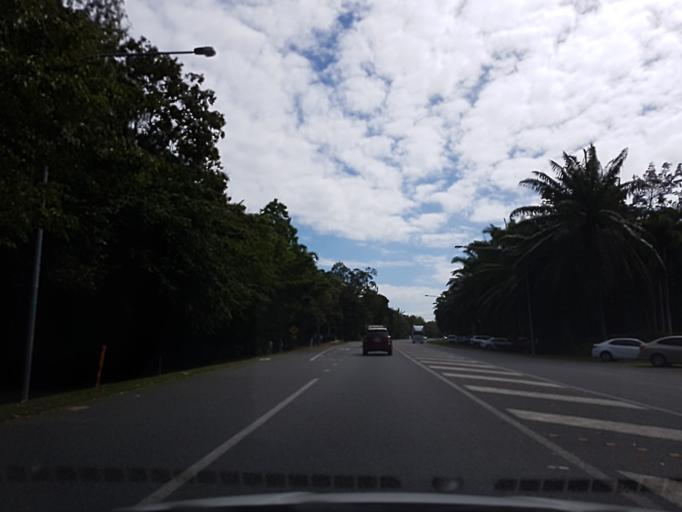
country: AU
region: Queensland
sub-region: Cairns
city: Port Douglas
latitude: -16.5159
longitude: 145.4648
